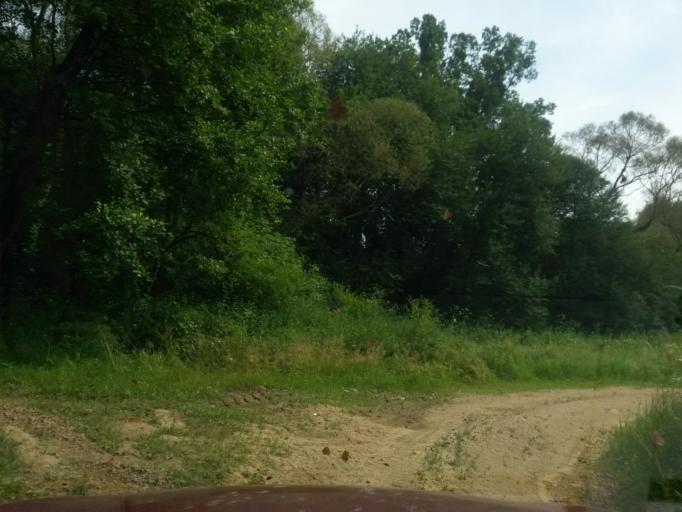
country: SK
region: Kosicky
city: Moldava nad Bodvou
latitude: 48.6503
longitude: 21.1074
